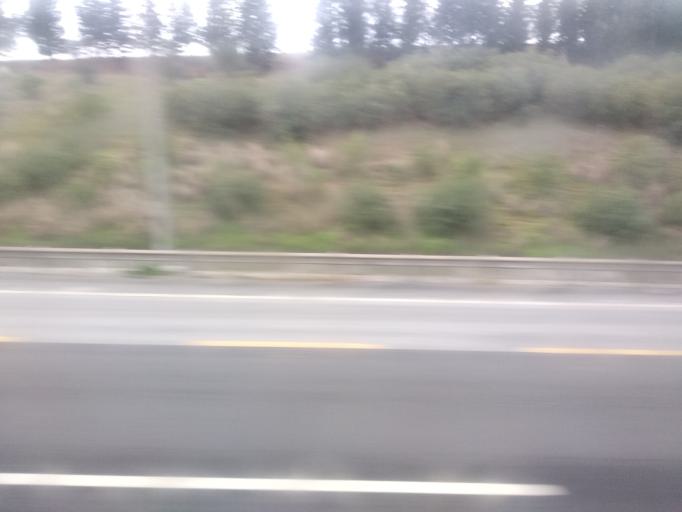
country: TR
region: Mersin
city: Yenice
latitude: 37.0366
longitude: 35.1748
